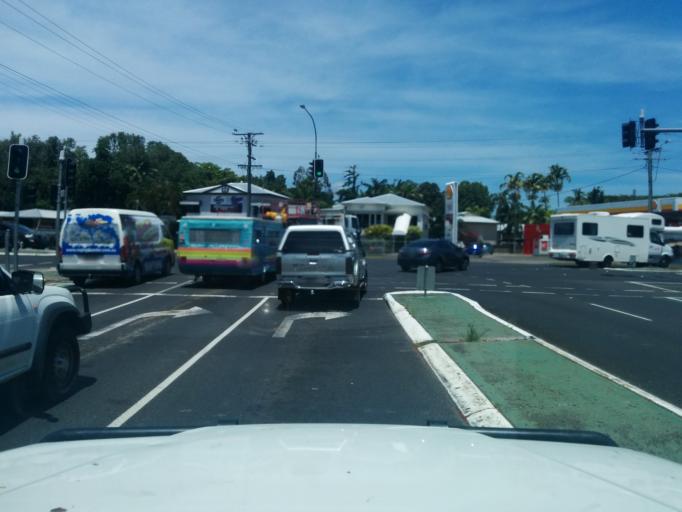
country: AU
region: Queensland
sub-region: Cairns
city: Cairns
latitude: -16.9185
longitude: 145.7403
